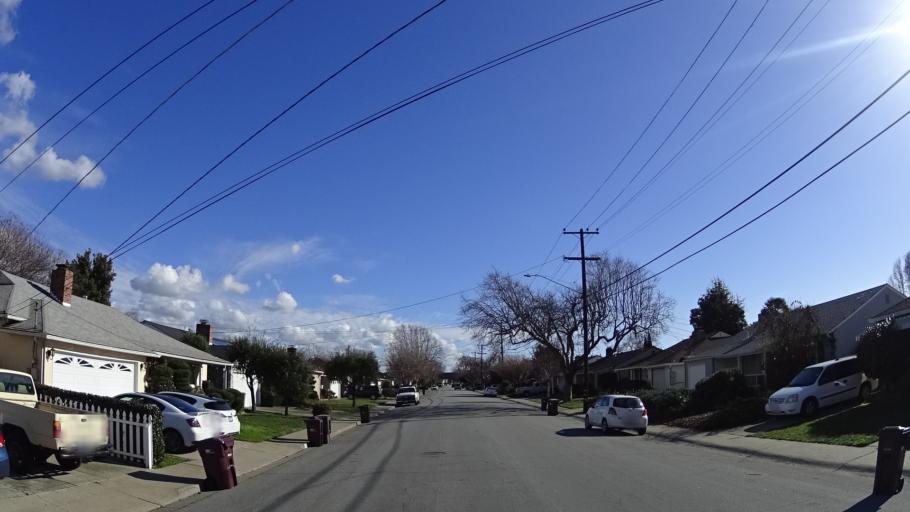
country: US
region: California
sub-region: Alameda County
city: San Lorenzo
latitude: 37.6807
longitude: -122.1197
